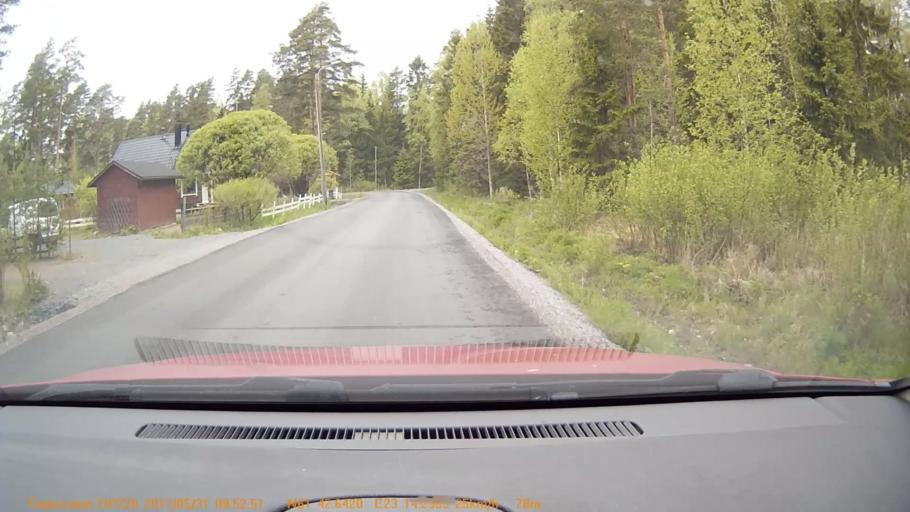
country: FI
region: Pirkanmaa
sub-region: Tampere
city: Viljakkala
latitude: 61.7107
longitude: 23.2384
